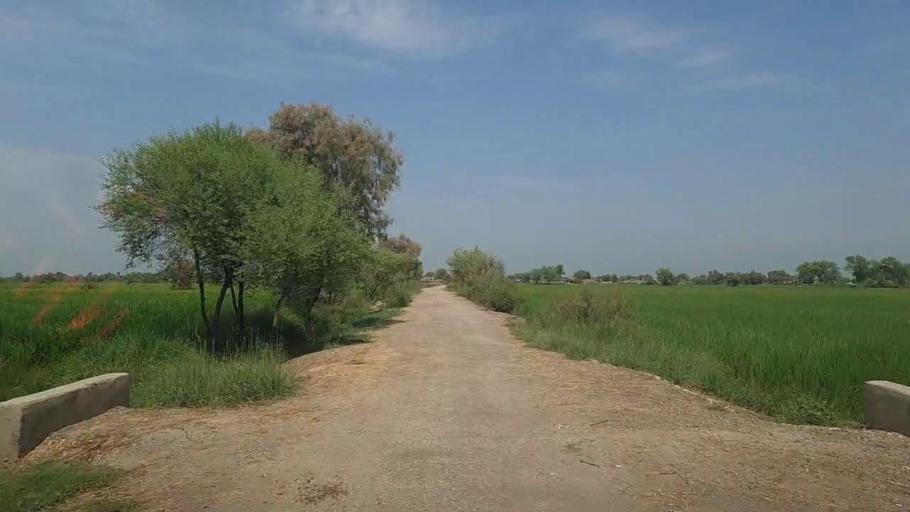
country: PK
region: Sindh
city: Thul
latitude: 28.3030
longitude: 68.6827
